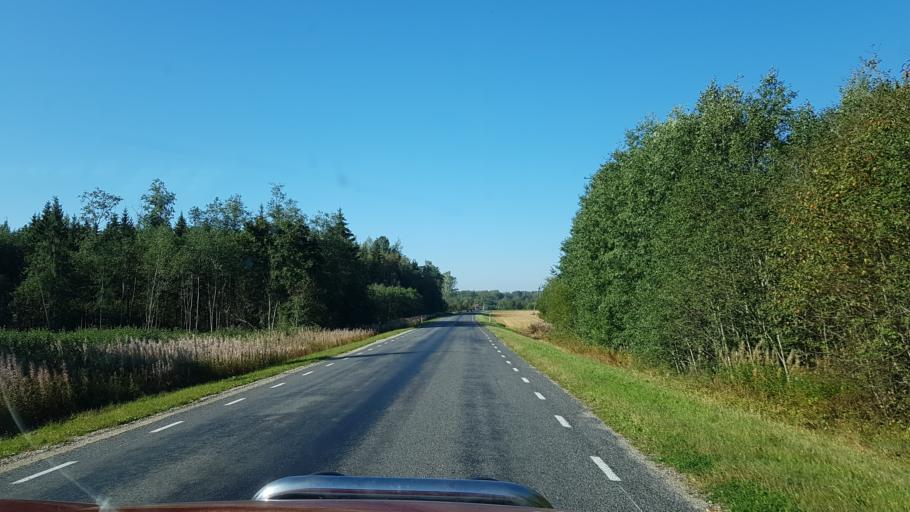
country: EE
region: Jogevamaa
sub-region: Jogeva linn
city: Jogeva
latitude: 58.6921
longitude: 26.3636
